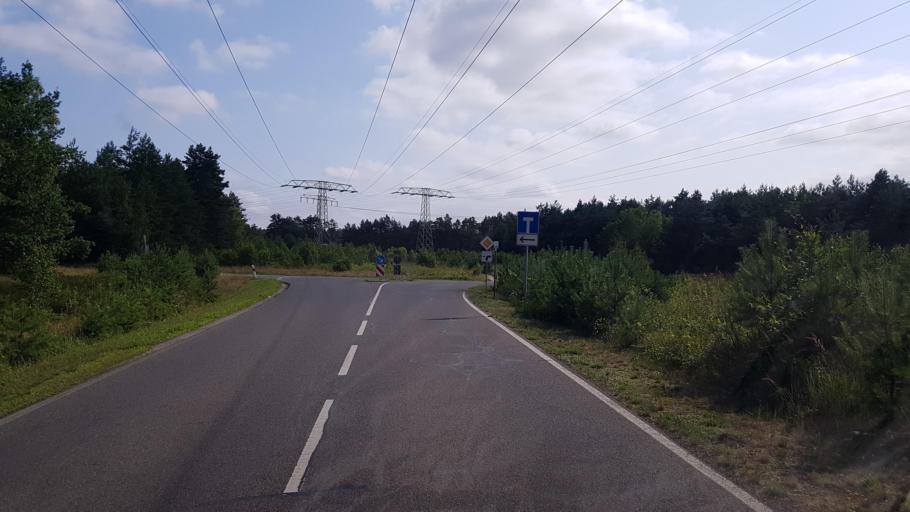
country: DE
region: Brandenburg
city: Grossraschen
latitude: 51.5958
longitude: 14.0235
